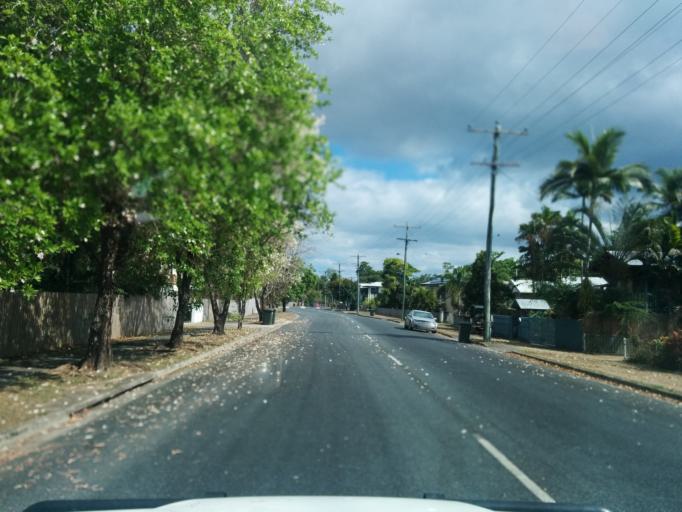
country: AU
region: Queensland
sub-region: Cairns
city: Cairns
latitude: -16.9086
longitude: 145.7555
